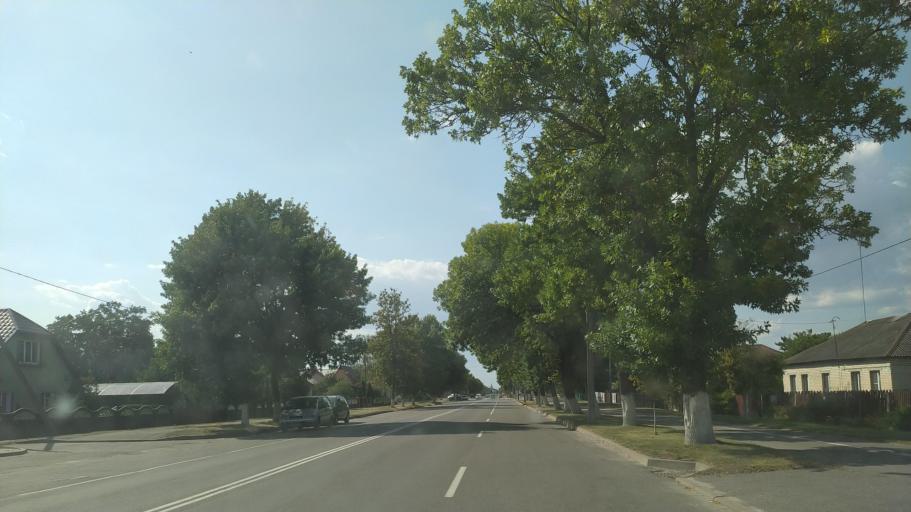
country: BY
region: Brest
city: Drahichyn
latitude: 52.1846
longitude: 25.1682
